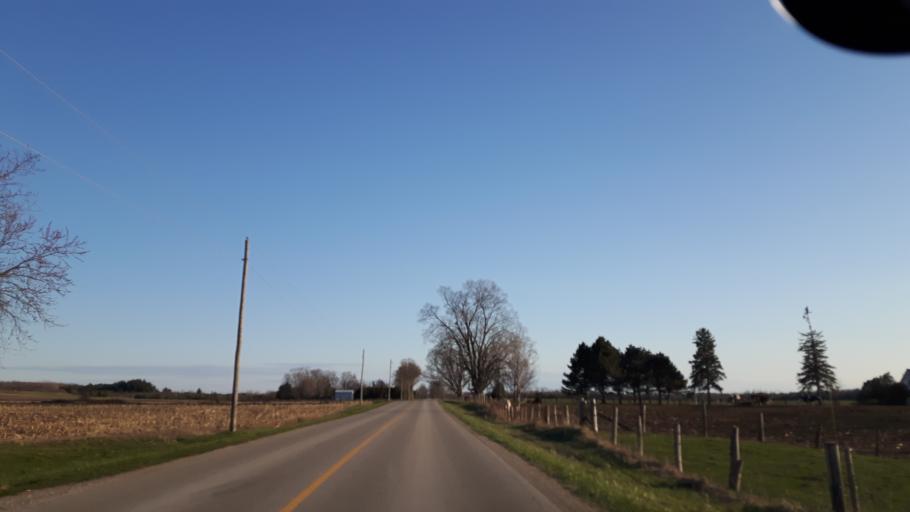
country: CA
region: Ontario
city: Goderich
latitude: 43.6664
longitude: -81.6847
